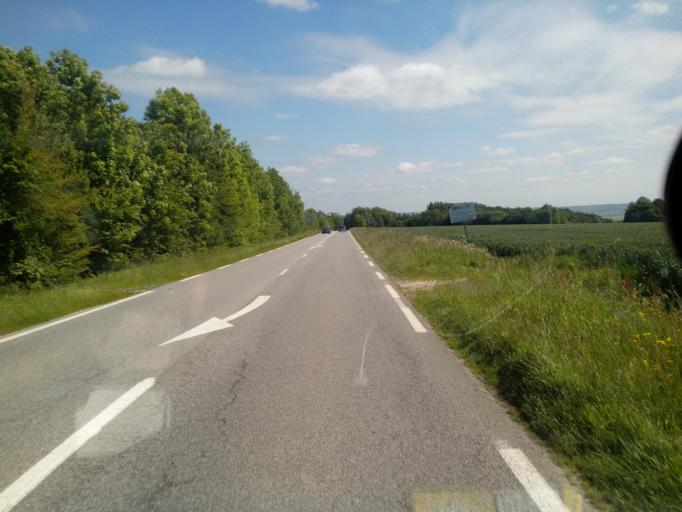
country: FR
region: Haute-Normandie
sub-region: Departement de la Seine-Maritime
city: Tancarville
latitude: 49.4953
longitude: 0.4376
